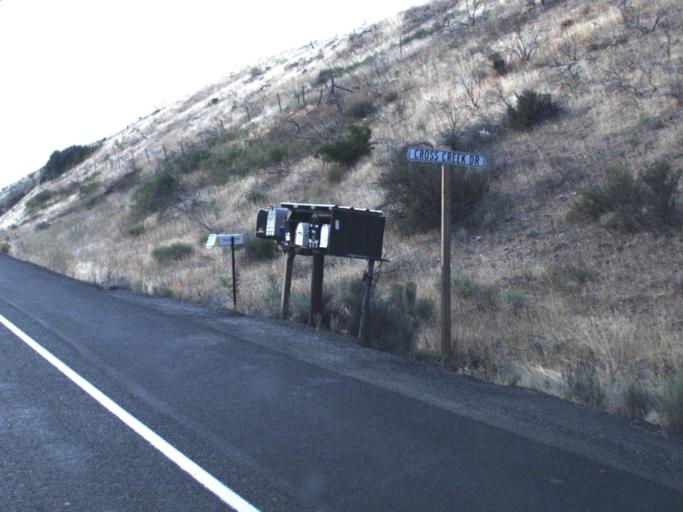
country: US
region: Washington
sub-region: Kittitas County
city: Ellensburg
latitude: 47.0854
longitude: -120.6457
